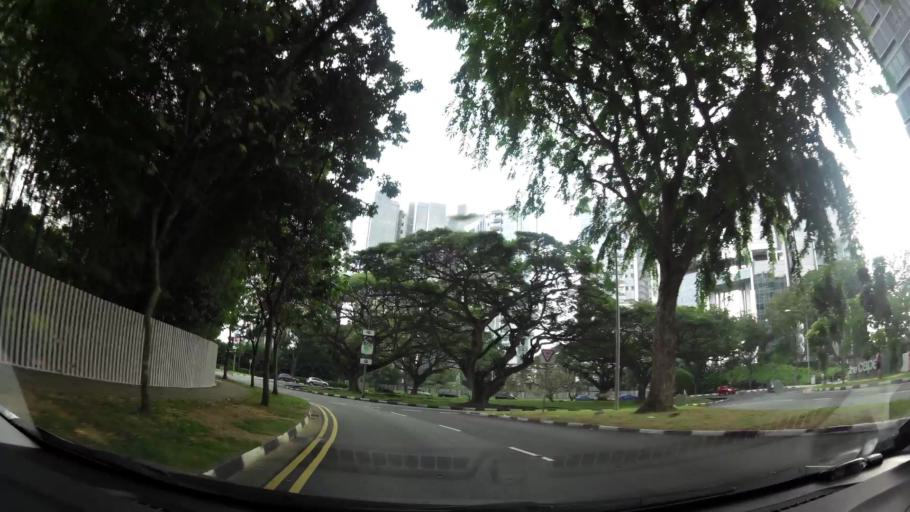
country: SG
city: Singapore
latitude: 1.3008
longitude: 103.9017
